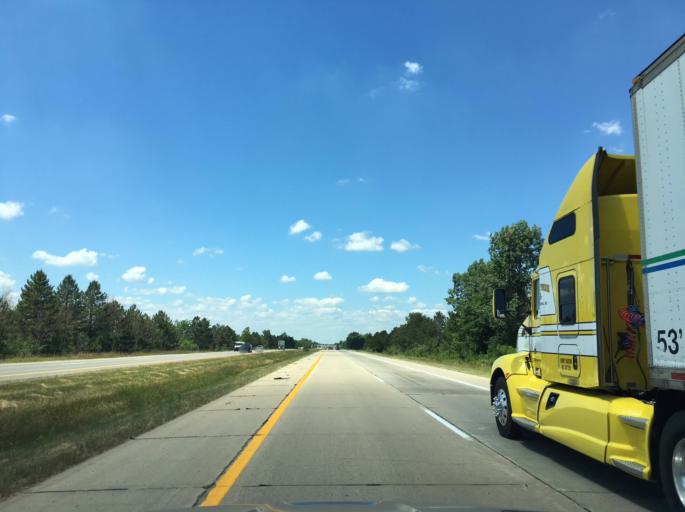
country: US
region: Michigan
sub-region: Bay County
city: Auburn
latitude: 43.5974
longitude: -84.1122
